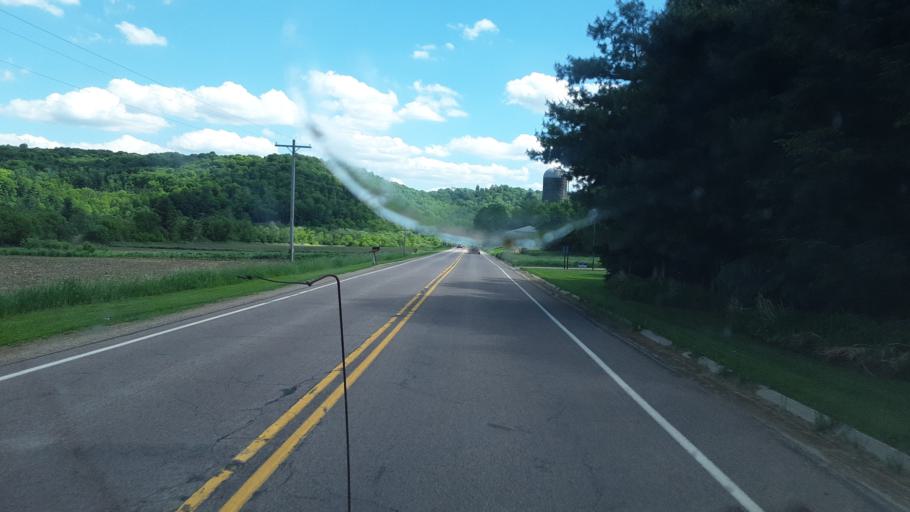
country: US
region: Wisconsin
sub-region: Richland County
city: Richland Center
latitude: 43.4007
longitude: -90.2431
